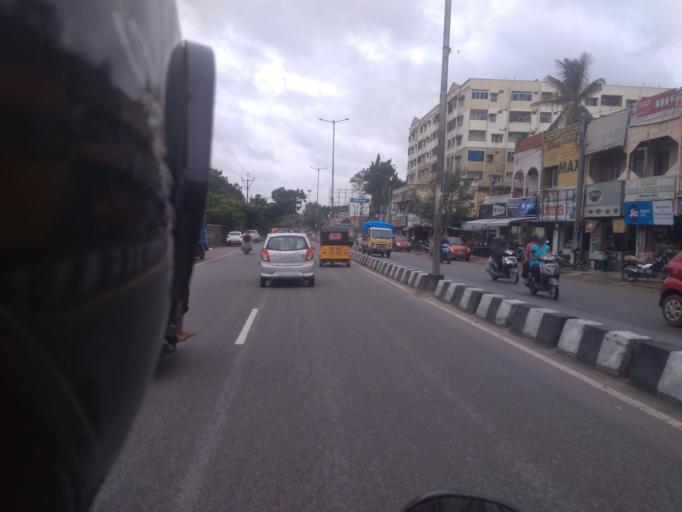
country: IN
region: Telangana
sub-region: Rangareddi
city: Secunderabad
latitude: 17.5005
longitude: 78.5138
